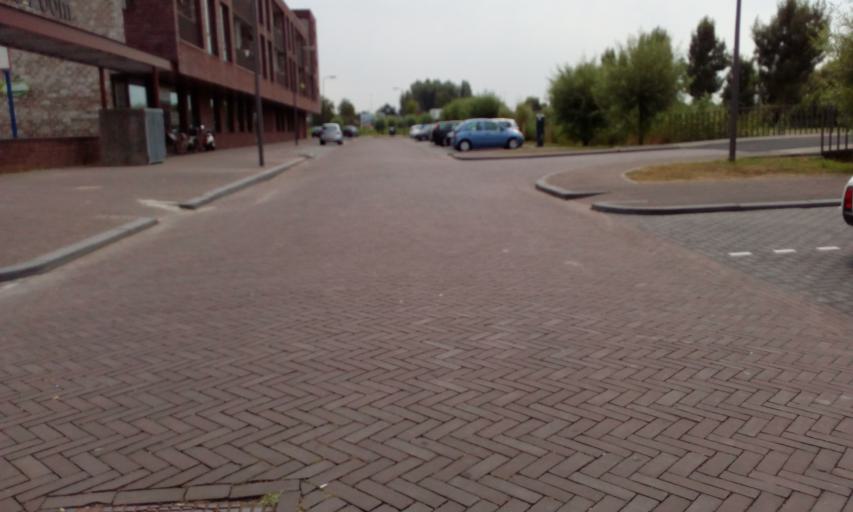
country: NL
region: South Holland
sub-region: Gemeente Krimpen aan den IJssel
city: Krimpen aan den IJssel
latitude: 51.9532
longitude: 4.6110
